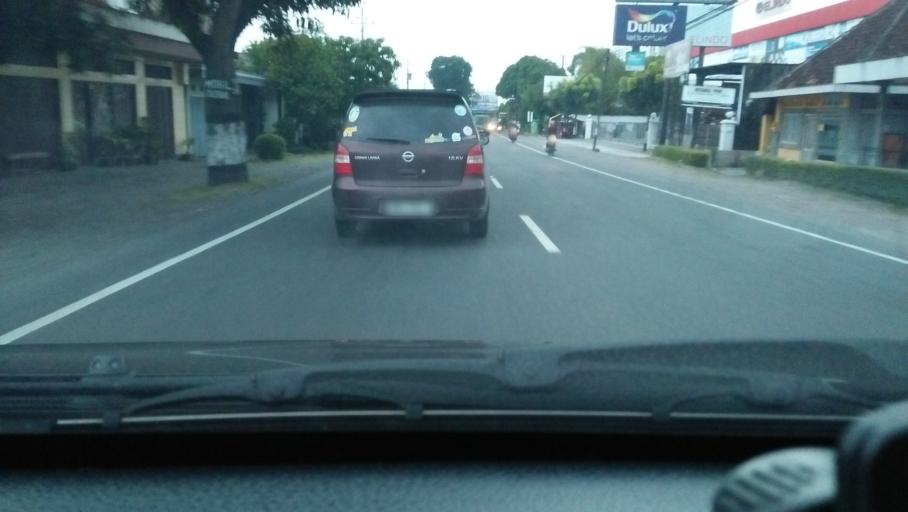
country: ID
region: Central Java
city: Magelang
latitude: -7.4281
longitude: 110.2298
